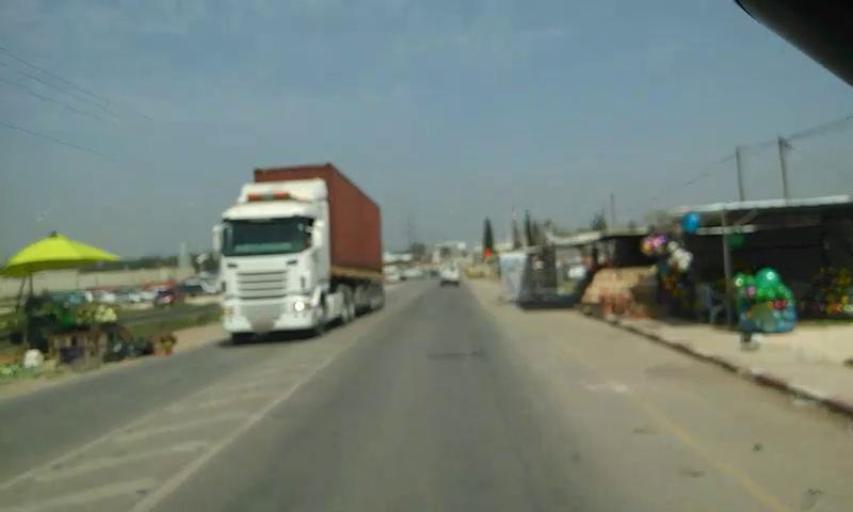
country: PS
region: West Bank
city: Al Jalamah
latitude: 32.5086
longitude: 35.3068
